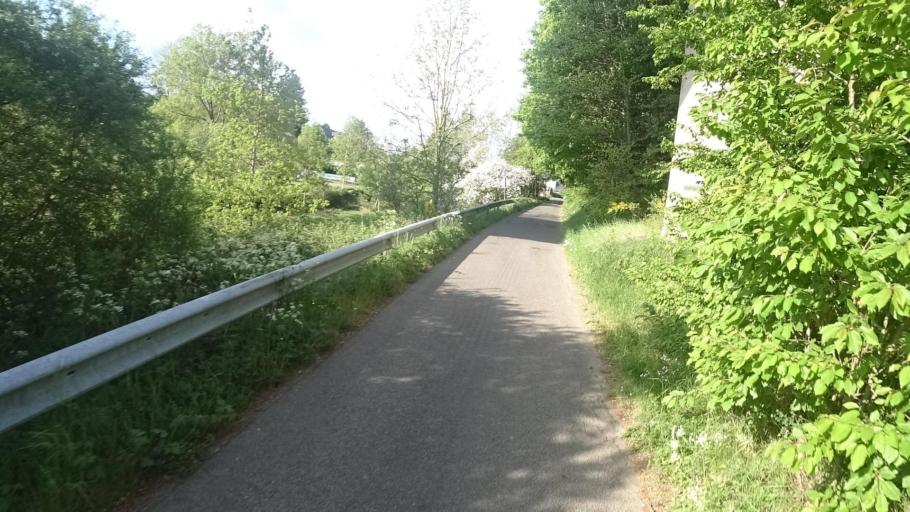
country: DE
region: Rheinland-Pfalz
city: Kirchsahr
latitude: 50.5142
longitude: 6.8708
